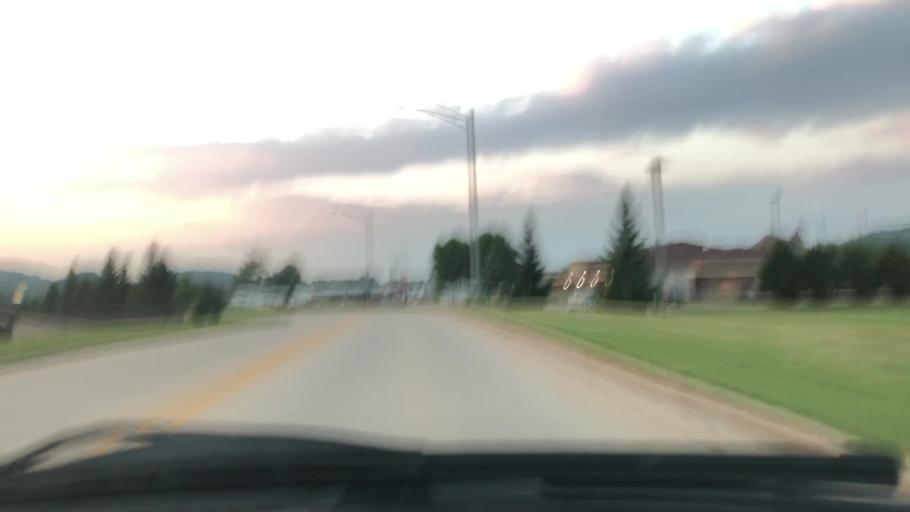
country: US
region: Wisconsin
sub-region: Richland County
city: Richland Center
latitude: 43.3315
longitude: -90.3878
